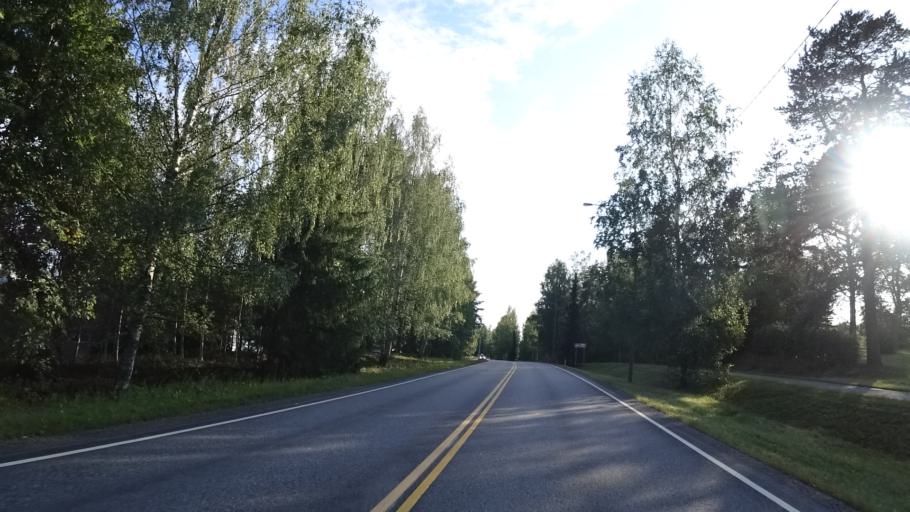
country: FI
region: South Karelia
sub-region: Imatra
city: Parikkala
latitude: 61.6054
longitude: 29.4860
